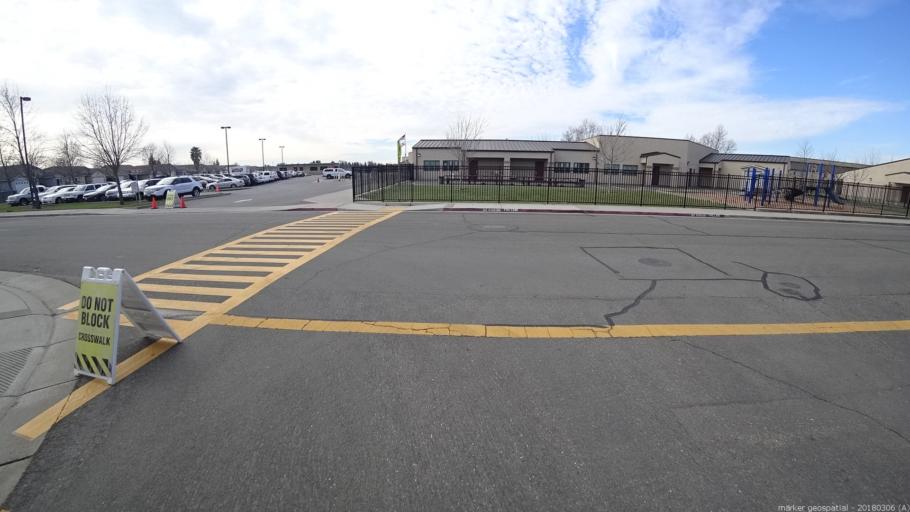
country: US
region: California
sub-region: Sacramento County
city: Vineyard
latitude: 38.4714
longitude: -121.3238
